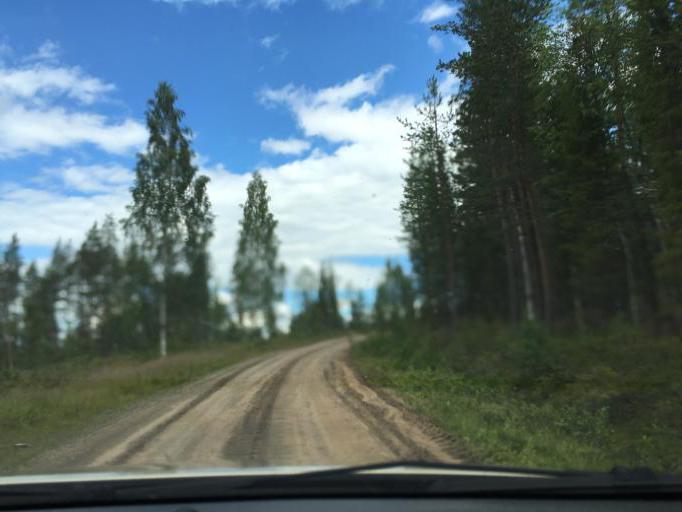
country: SE
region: Norrbotten
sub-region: Overkalix Kommun
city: OEverkalix
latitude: 66.1444
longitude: 22.7881
